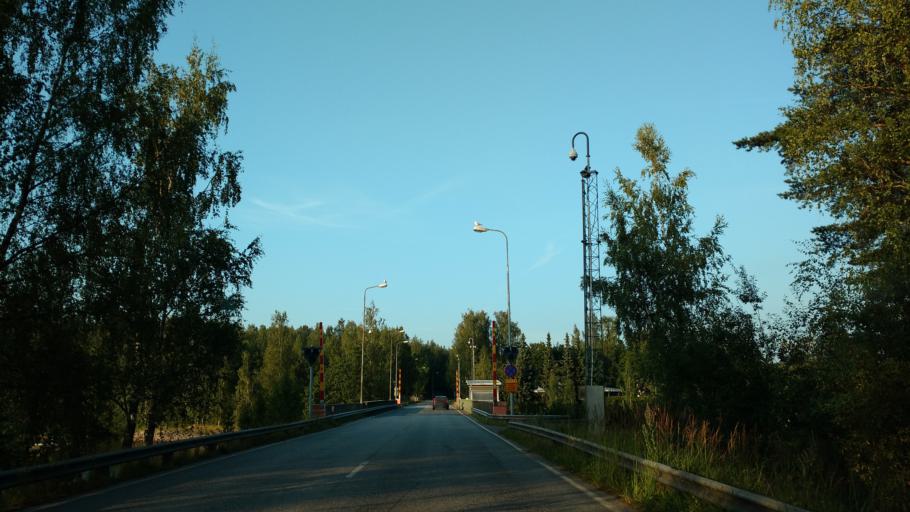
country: FI
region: Varsinais-Suomi
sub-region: Salo
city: Saerkisalo
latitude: 60.1874
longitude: 22.8672
